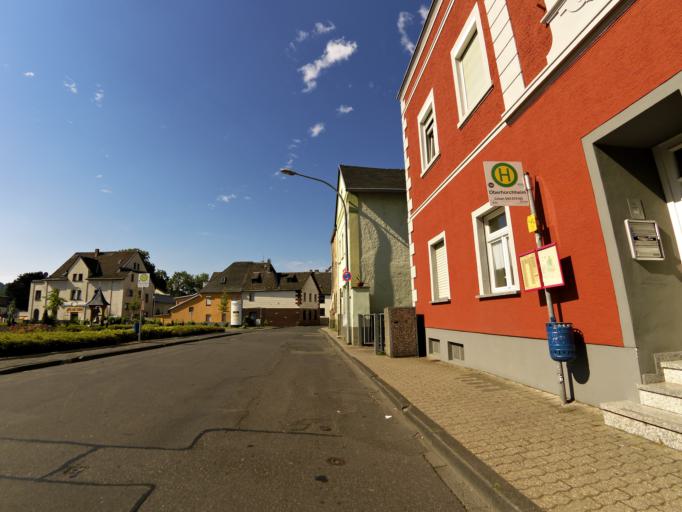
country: DE
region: Rheinland-Pfalz
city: Koblenz
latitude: 50.3262
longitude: 7.5957
